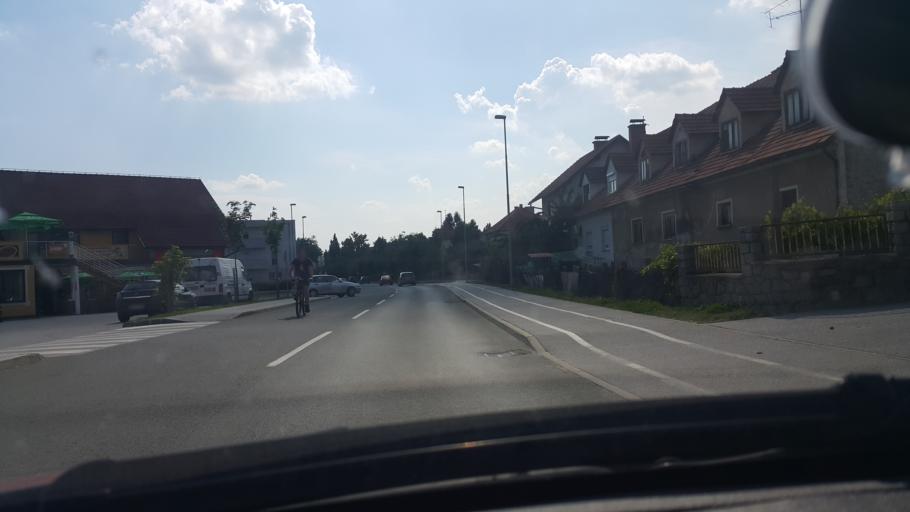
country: SI
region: Ptuj
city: Ptuj
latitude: 46.4283
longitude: 15.8835
